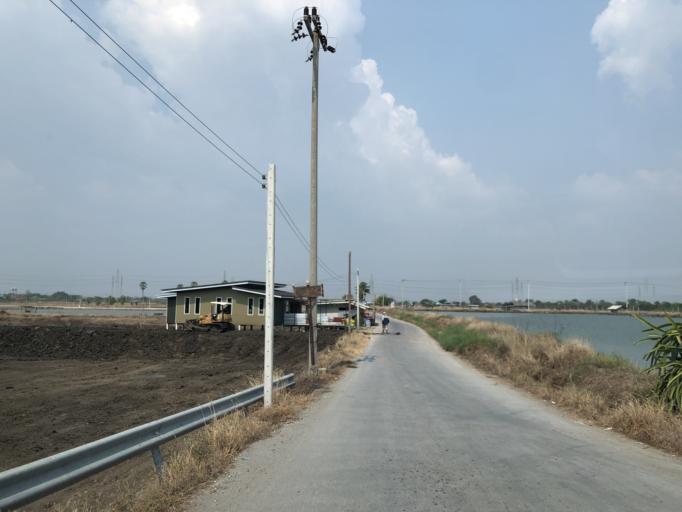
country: TH
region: Samut Prakan
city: Bang Bo
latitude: 13.5386
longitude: 100.8792
